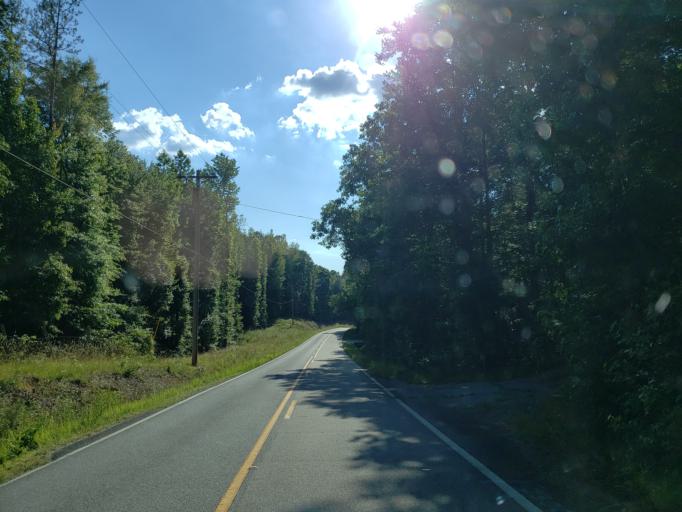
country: US
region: Georgia
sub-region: Carroll County
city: Carrollton
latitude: 33.6499
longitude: -85.0940
